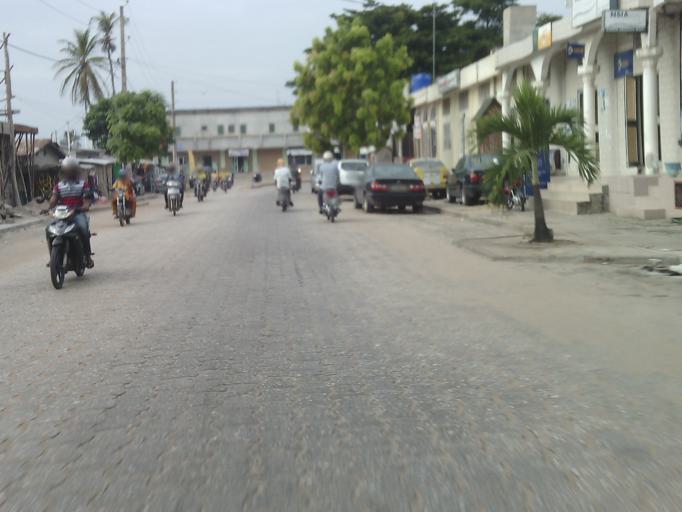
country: BJ
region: Littoral
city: Cotonou
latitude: 6.3886
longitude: 2.3764
